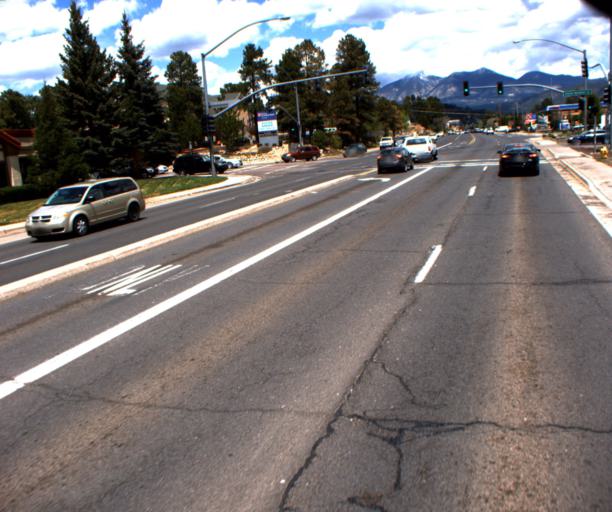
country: US
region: Arizona
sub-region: Coconino County
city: Flagstaff
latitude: 35.1785
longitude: -111.6612
